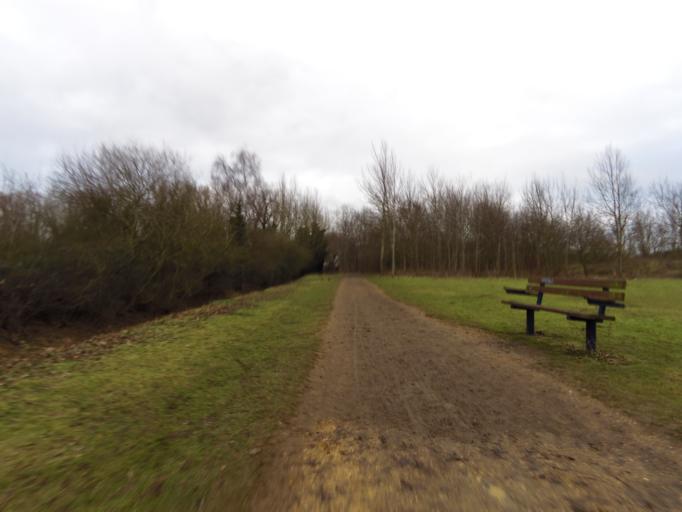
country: GB
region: England
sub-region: Cambridgeshire
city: Waterbeach
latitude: 52.2361
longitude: 0.1661
